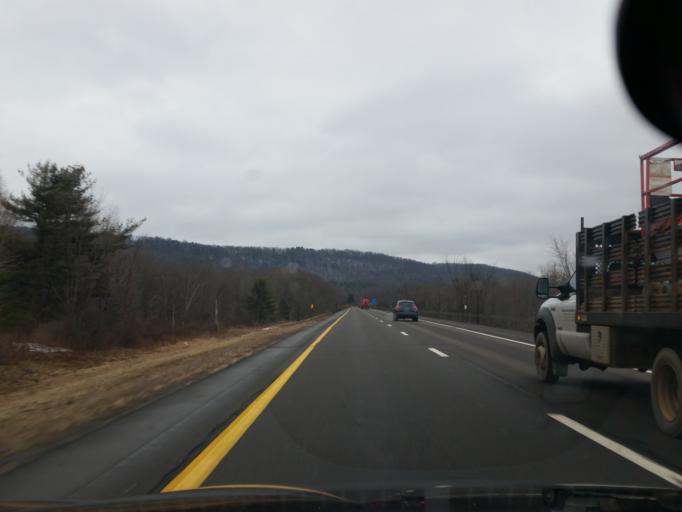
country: US
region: Pennsylvania
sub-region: Susquehanna County
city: Hallstead
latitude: 42.0101
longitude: -75.7613
